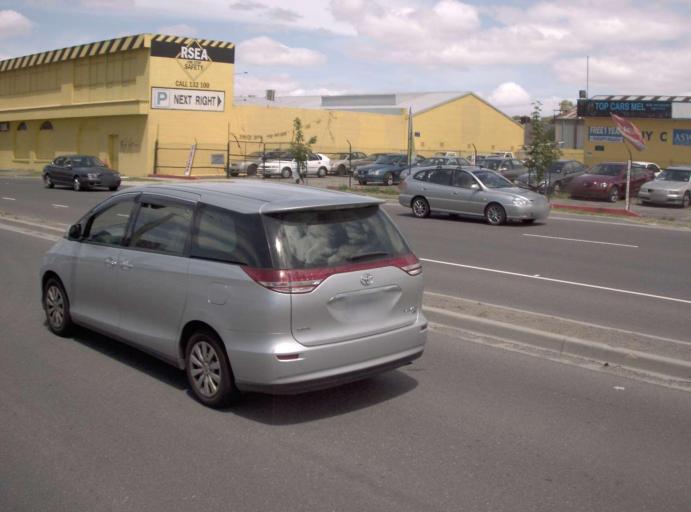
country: AU
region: Victoria
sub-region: Greater Dandenong
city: Dandenong
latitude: -37.9911
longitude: 145.2081
